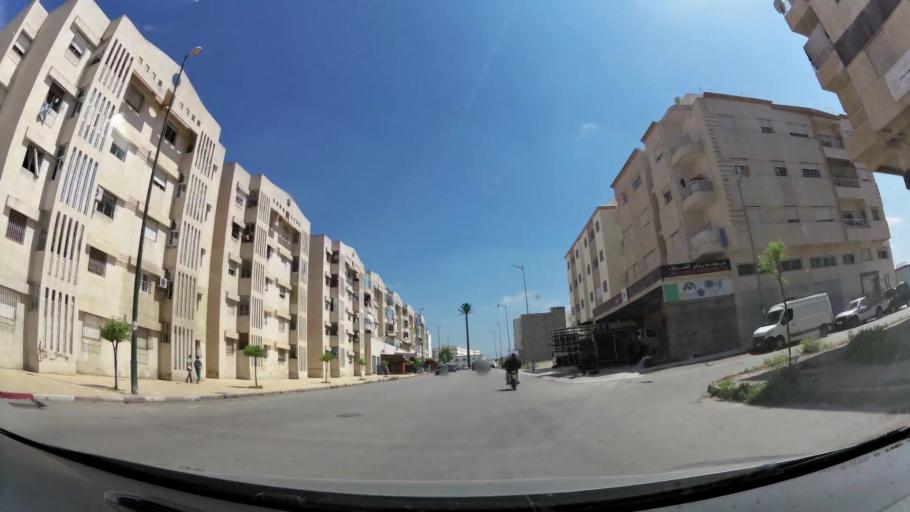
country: MA
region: Fes-Boulemane
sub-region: Fes
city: Fes
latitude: 34.0136
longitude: -5.0440
